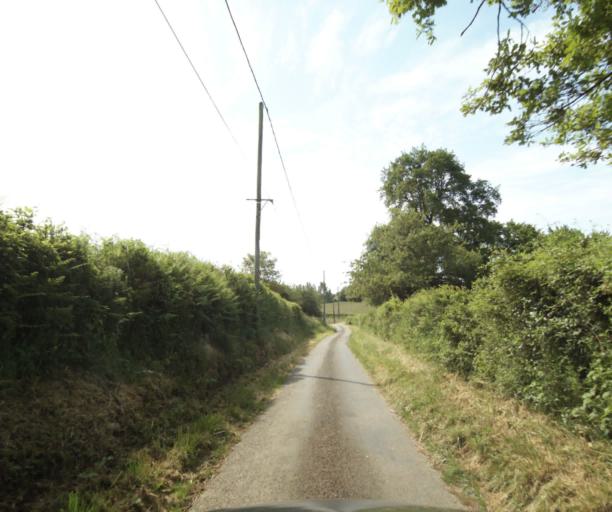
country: FR
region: Bourgogne
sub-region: Departement de Saone-et-Loire
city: Gueugnon
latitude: 46.5416
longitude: 4.1235
